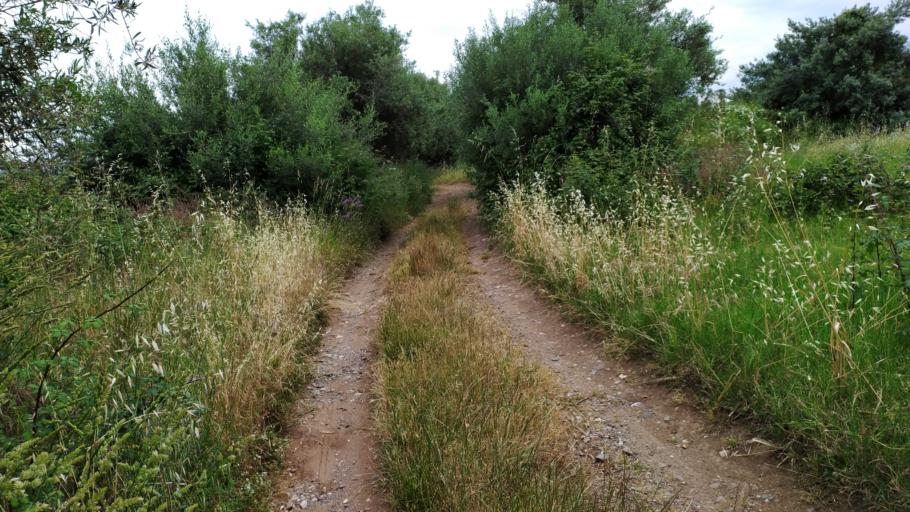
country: IT
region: Sicily
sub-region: Messina
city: San Filippo del Mela
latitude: 38.1819
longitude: 15.2642
